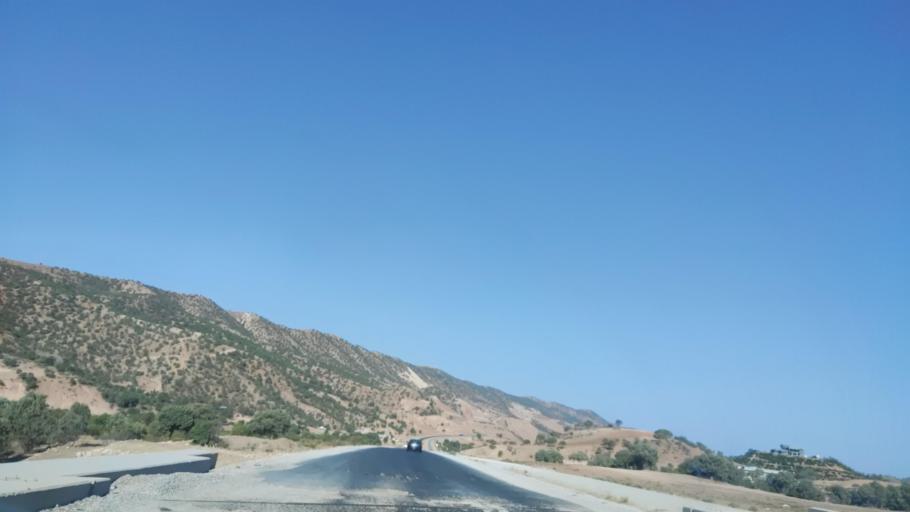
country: IQ
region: Arbil
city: Shaqlawah
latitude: 36.4302
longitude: 44.3256
